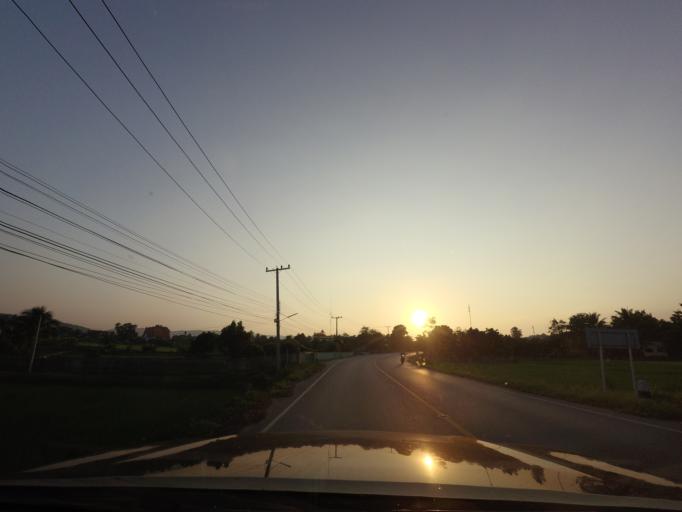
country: TH
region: Nan
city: Na Noi
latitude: 18.3262
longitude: 100.7209
